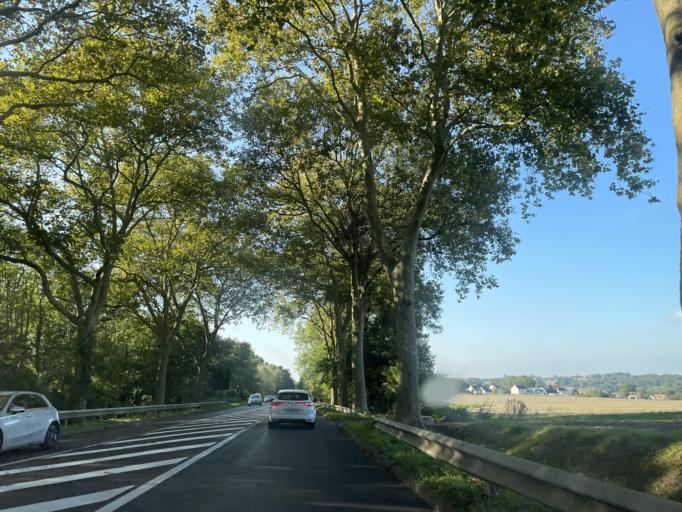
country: FR
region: Ile-de-France
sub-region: Departement de Seine-et-Marne
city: La Chapelle-sur-Crecy
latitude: 48.8485
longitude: 2.9394
